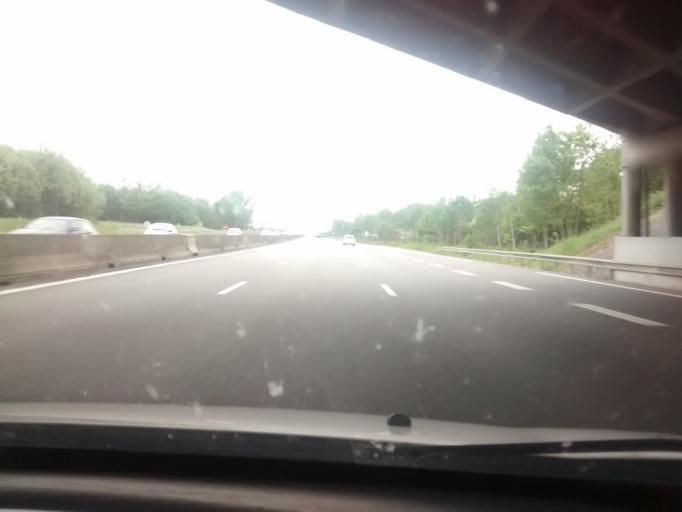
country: FR
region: Centre
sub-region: Departement d'Eure-et-Loir
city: Gasville-Oiseme
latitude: 48.4552
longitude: 1.5390
